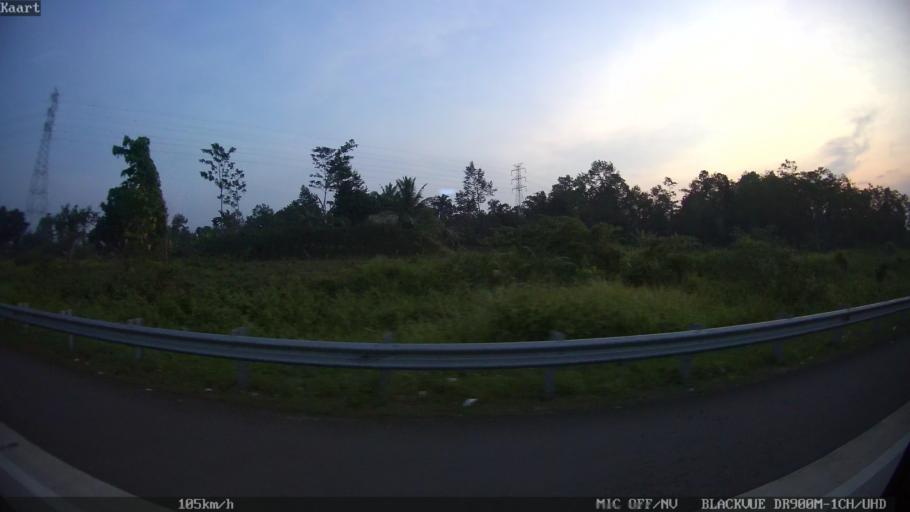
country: ID
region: Lampung
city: Pasuruan
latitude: -5.7184
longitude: 105.6606
